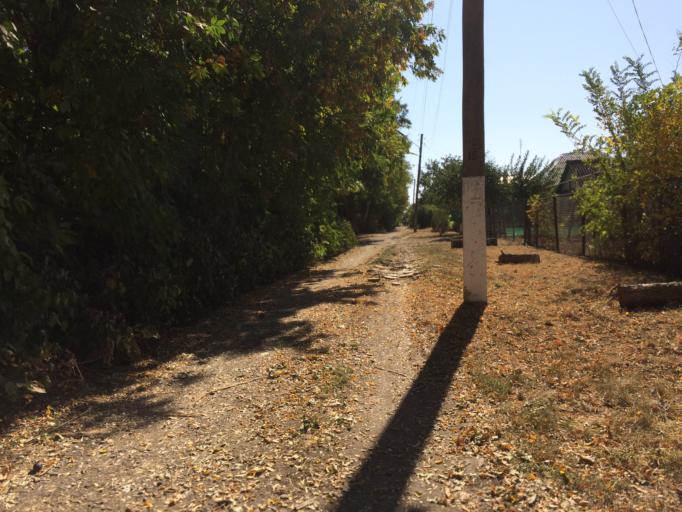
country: RU
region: Rostov
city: Gigant
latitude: 46.5185
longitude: 41.1877
